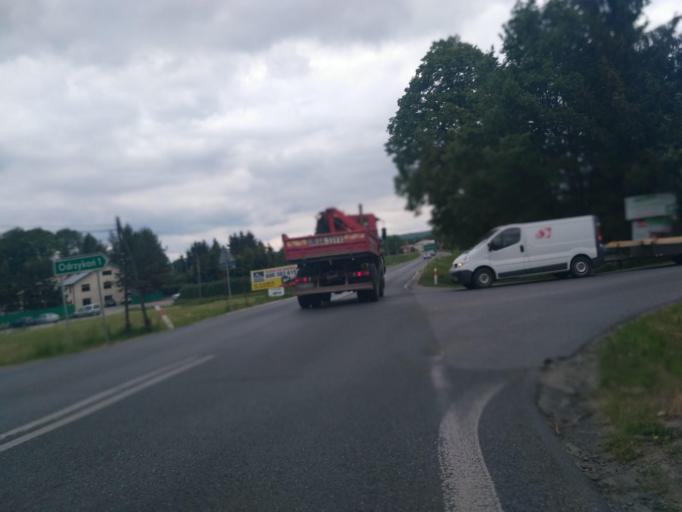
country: PL
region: Subcarpathian Voivodeship
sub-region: Powiat krosnienski
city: Odrzykon
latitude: 49.7311
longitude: 21.7116
